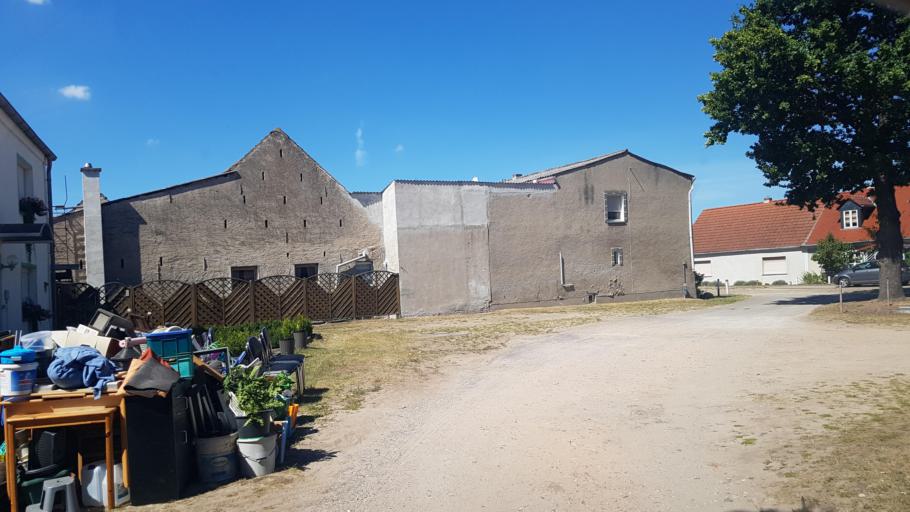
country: DE
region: Brandenburg
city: Bruck
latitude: 52.2468
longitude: 12.7019
